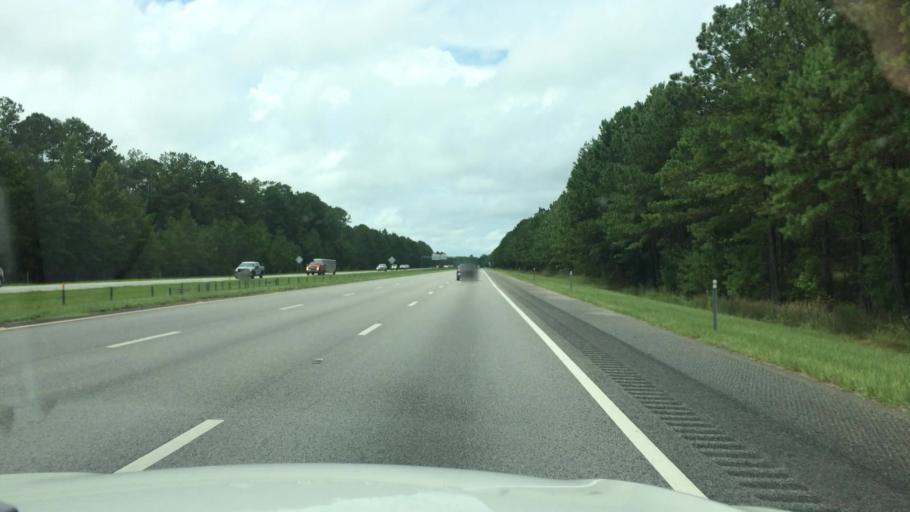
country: US
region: South Carolina
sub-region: Florence County
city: Florence
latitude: 34.1983
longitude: -79.8542
